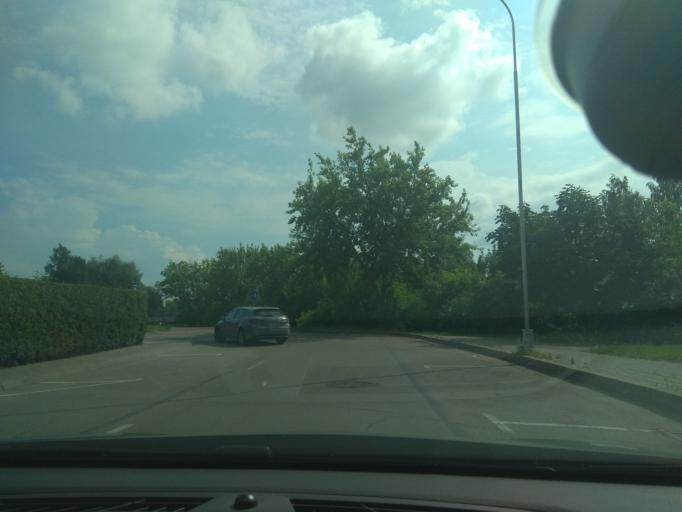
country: LT
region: Marijampoles apskritis
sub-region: Marijampole Municipality
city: Marijampole
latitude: 54.5649
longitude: 23.3469
